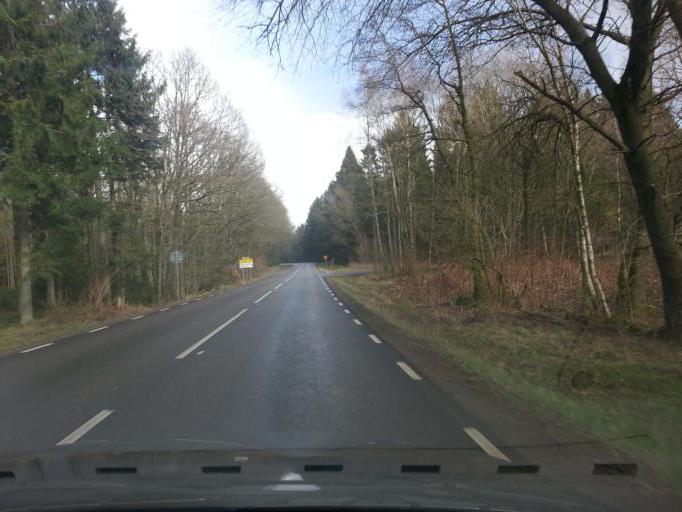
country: SE
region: Skane
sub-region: Astorps Kommun
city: Astorp
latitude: 56.1181
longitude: 12.9932
